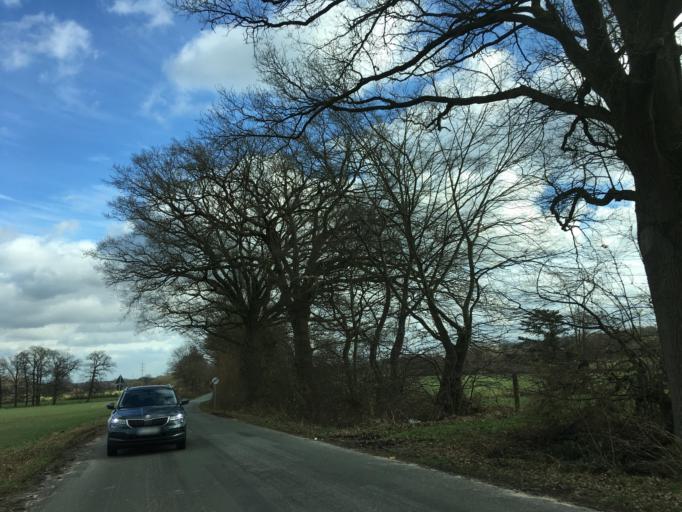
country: DE
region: North Rhine-Westphalia
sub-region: Regierungsbezirk Munster
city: Horstmar
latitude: 52.0792
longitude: 7.3221
